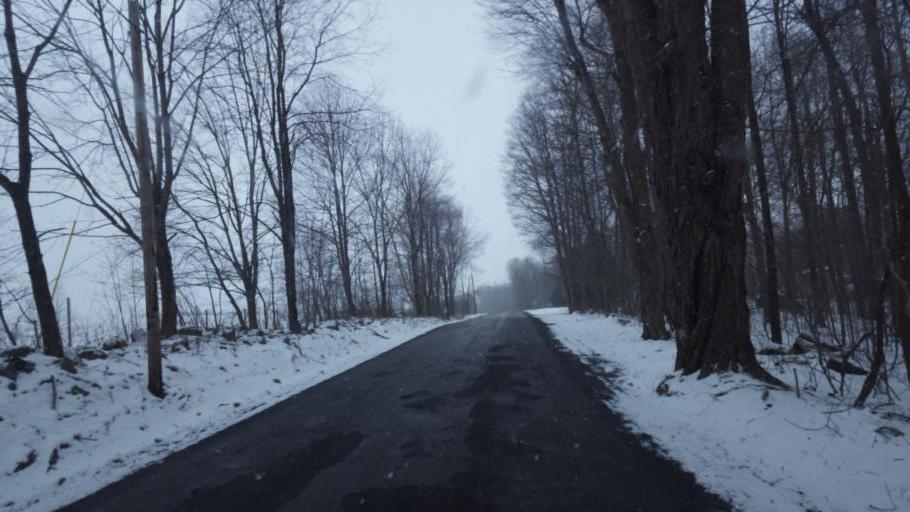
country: US
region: Pennsylvania
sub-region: Mercer County
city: Stoneboro
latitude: 41.4220
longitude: -80.0612
